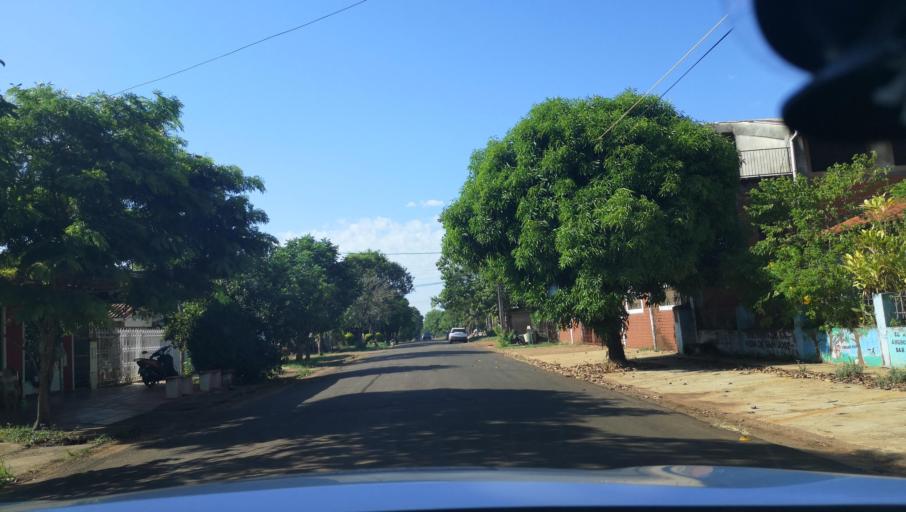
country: PY
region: Itapua
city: Carmen del Parana
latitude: -27.1669
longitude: -56.2360
